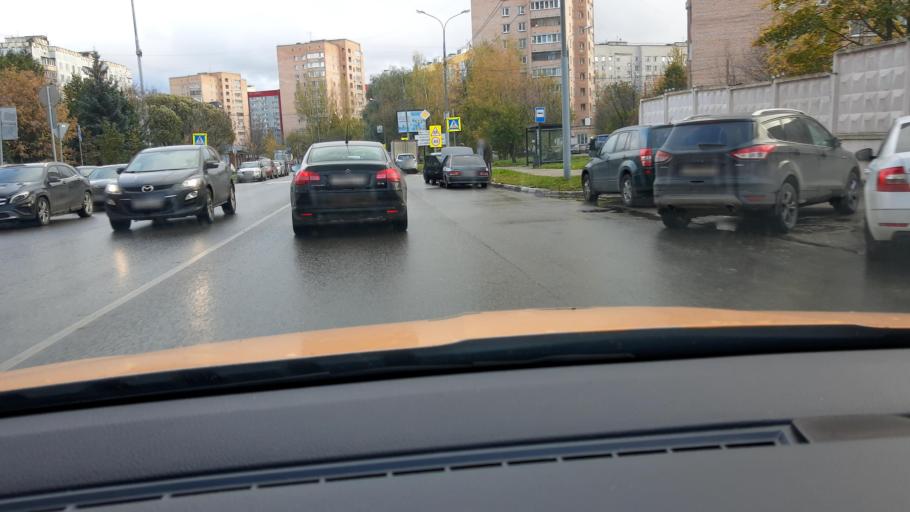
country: RU
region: Moskovskaya
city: Odintsovo
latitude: 55.6865
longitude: 37.2902
